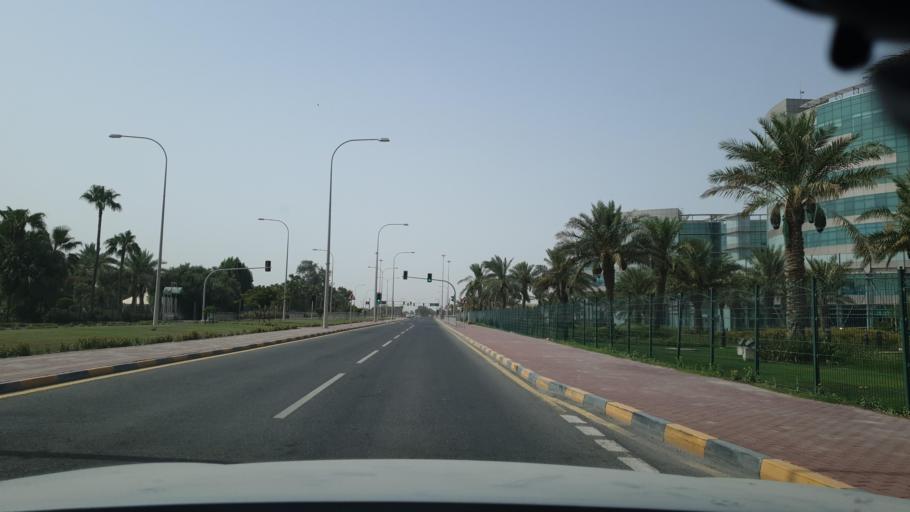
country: QA
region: Al Wakrah
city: Umm Sa'id
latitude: 24.9941
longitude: 51.5490
